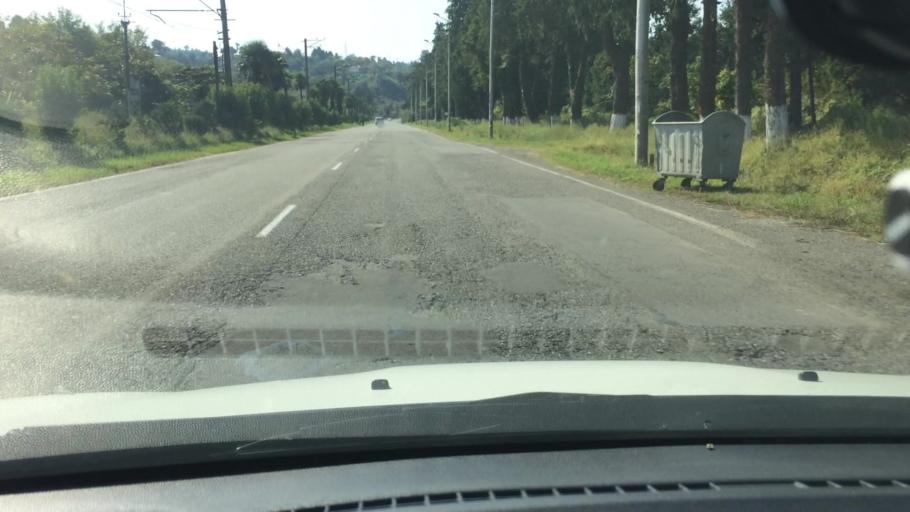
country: GE
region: Ajaria
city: Kobuleti
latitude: 41.7842
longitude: 41.7653
